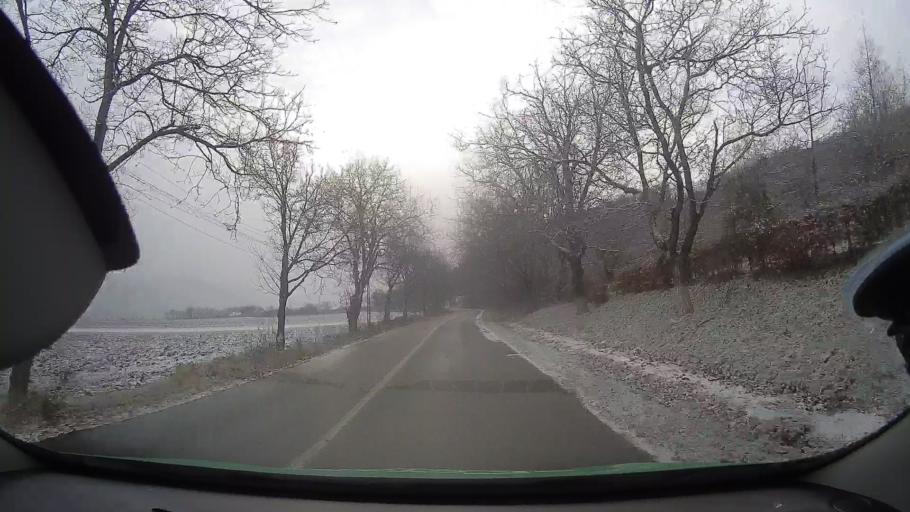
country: RO
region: Alba
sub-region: Comuna Rimetea
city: Rimetea
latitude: 46.4296
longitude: 23.5612
